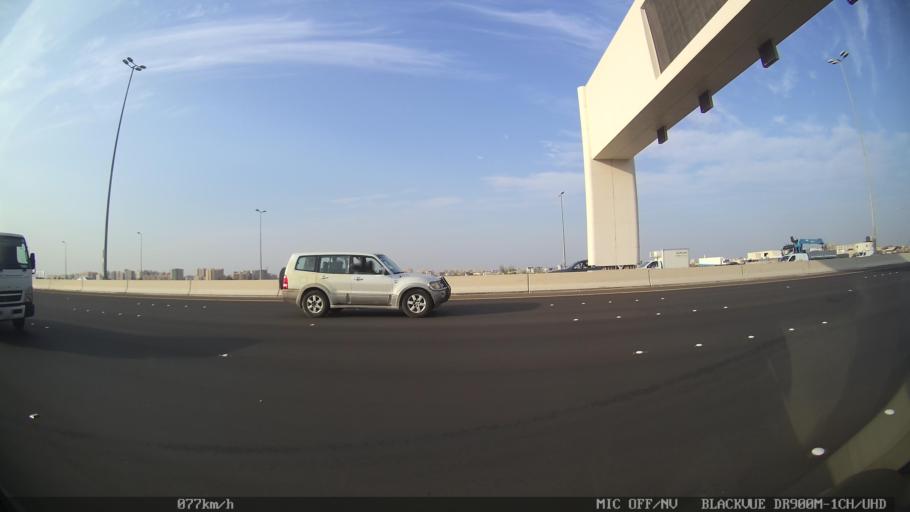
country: KW
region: Al Farwaniyah
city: Janub as Surrah
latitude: 29.2596
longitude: 47.9782
